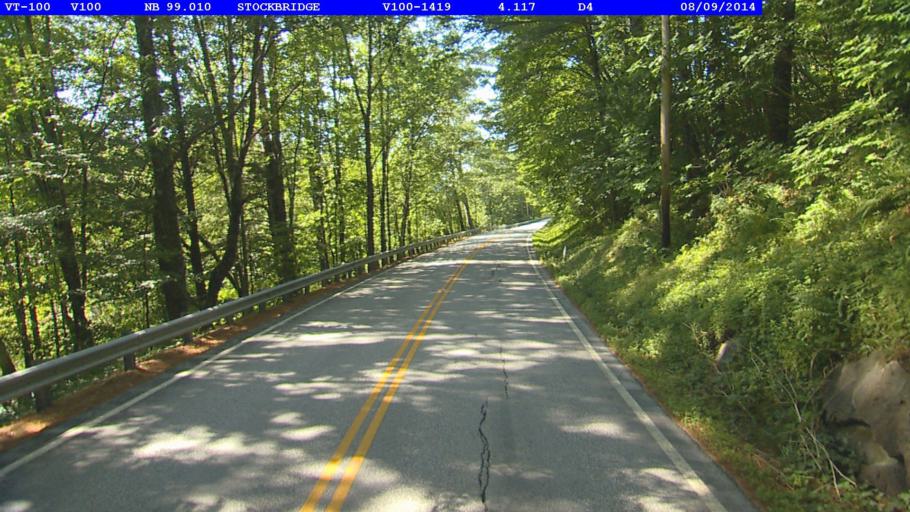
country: US
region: Vermont
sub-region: Orange County
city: Randolph
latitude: 43.7964
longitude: -72.7681
